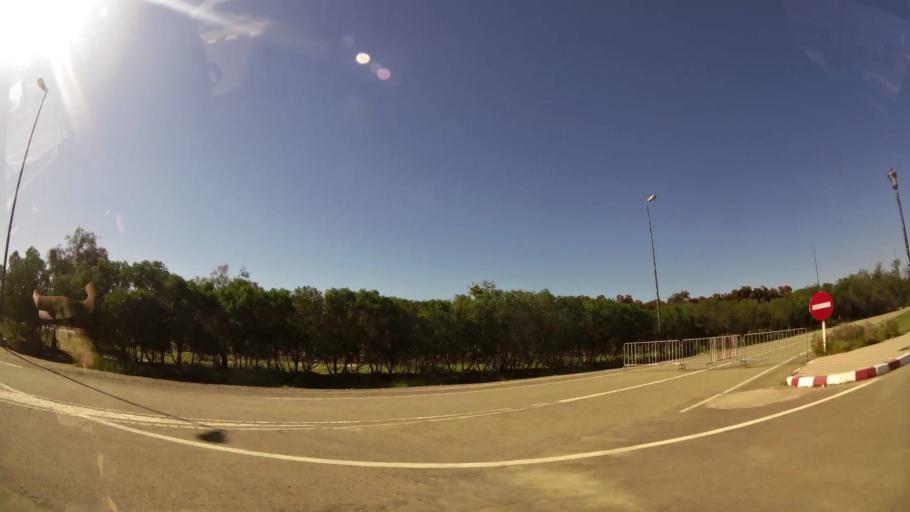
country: MA
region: Oriental
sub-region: Oujda-Angad
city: Oujda
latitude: 34.7828
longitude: -1.9472
